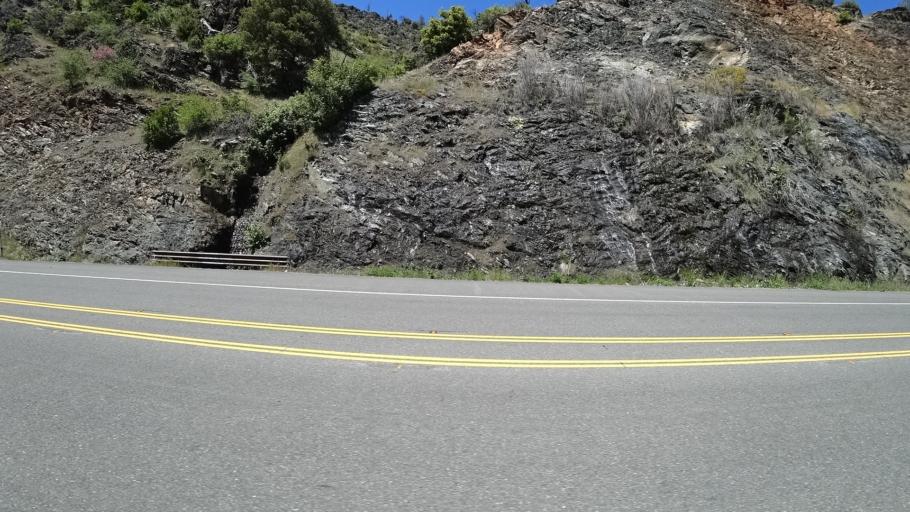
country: US
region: California
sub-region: Trinity County
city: Weaverville
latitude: 40.7424
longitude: -122.9994
